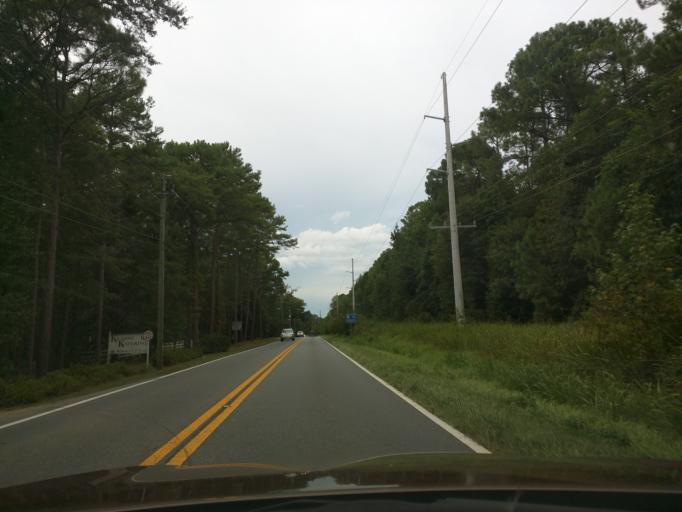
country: US
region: Florida
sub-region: Leon County
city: Tallahassee
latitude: 30.5807
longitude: -84.2404
